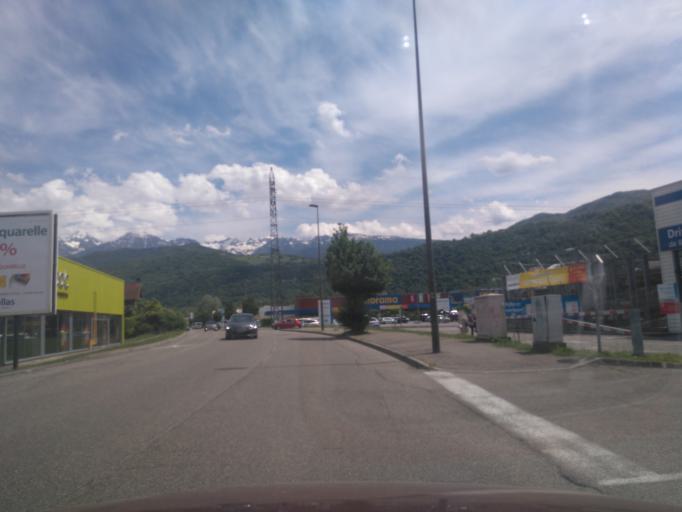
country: FR
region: Rhone-Alpes
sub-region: Departement de l'Isere
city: Gieres
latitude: 45.1848
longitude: 5.7714
